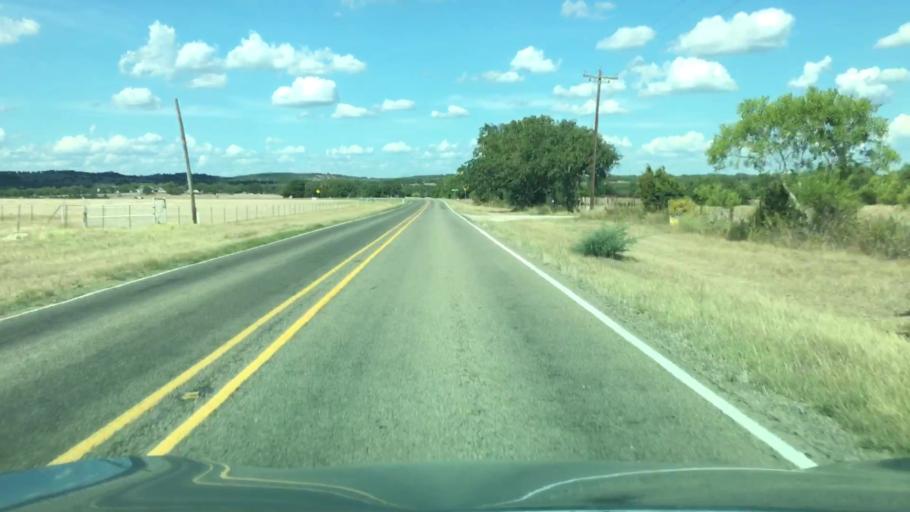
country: US
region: Texas
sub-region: Hays County
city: Dripping Springs
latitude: 30.1860
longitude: -98.2178
